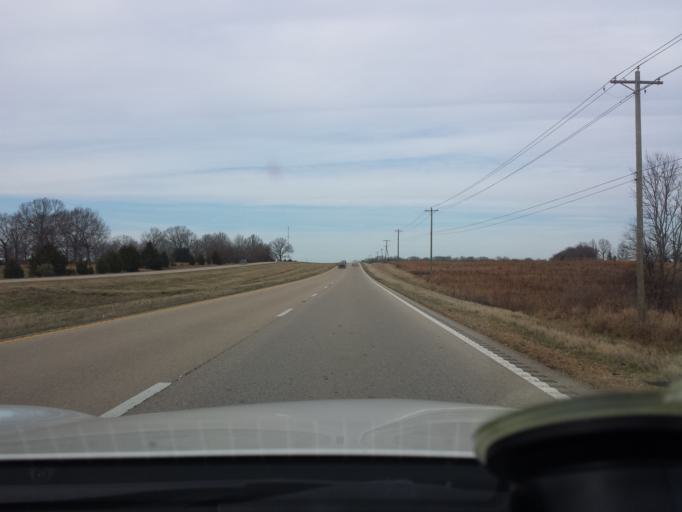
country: US
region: Mississippi
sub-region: Monroe County
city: Aberdeen
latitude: 33.7876
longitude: -88.6943
